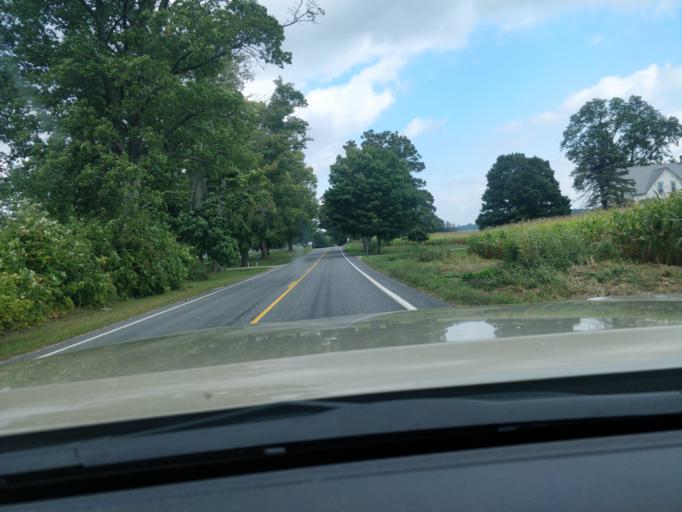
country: US
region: Michigan
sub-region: Kent County
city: Lowell
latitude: 42.8860
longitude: -85.2808
